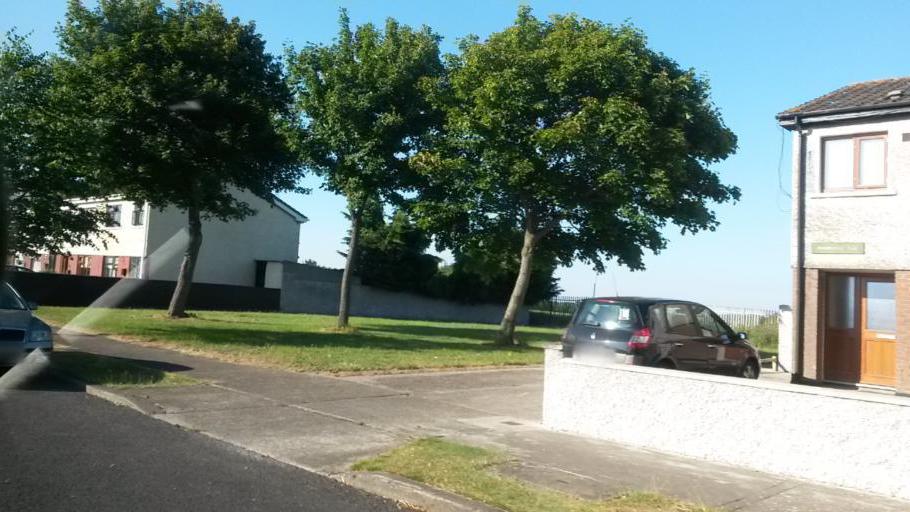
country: IE
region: Leinster
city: Ballymun
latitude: 53.4534
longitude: -6.2887
